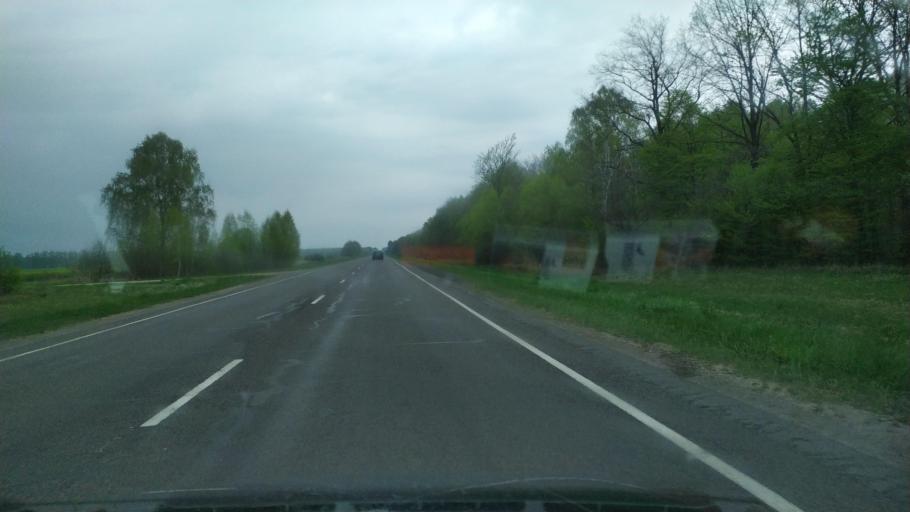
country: BY
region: Brest
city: Horad Kobryn
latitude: 52.3177
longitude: 24.5539
